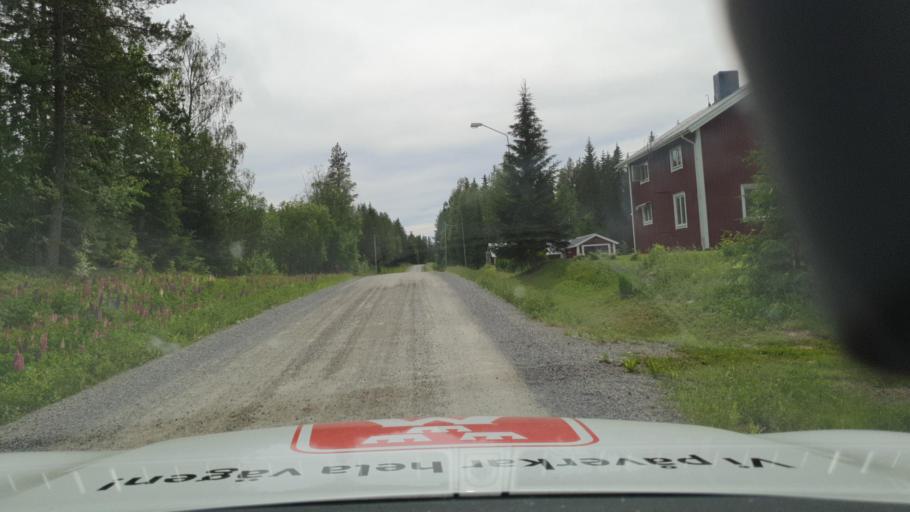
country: SE
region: Vaesterbotten
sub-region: Skelleftea Kommun
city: Burea
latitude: 64.4675
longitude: 21.0525
